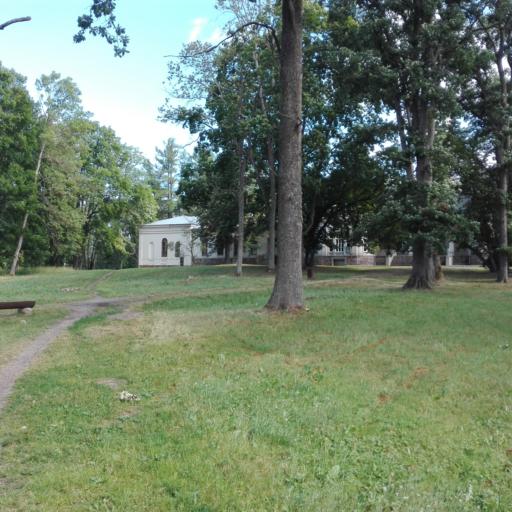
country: LT
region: Panevezys
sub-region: Birzai
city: Birzai
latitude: 56.2186
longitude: 24.7685
